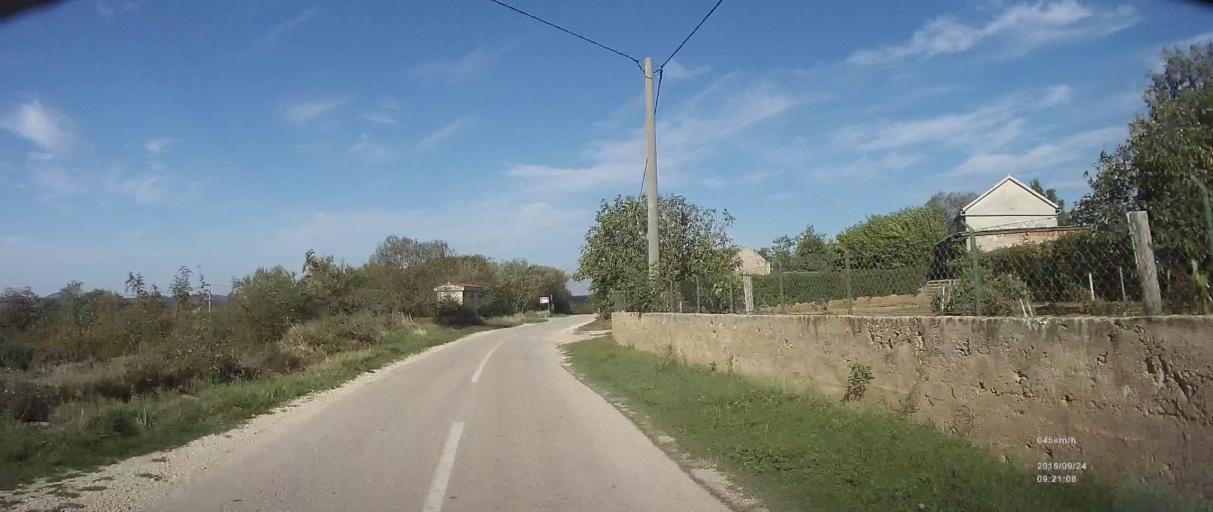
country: HR
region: Zadarska
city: Polaca
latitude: 44.0685
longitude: 15.4913
